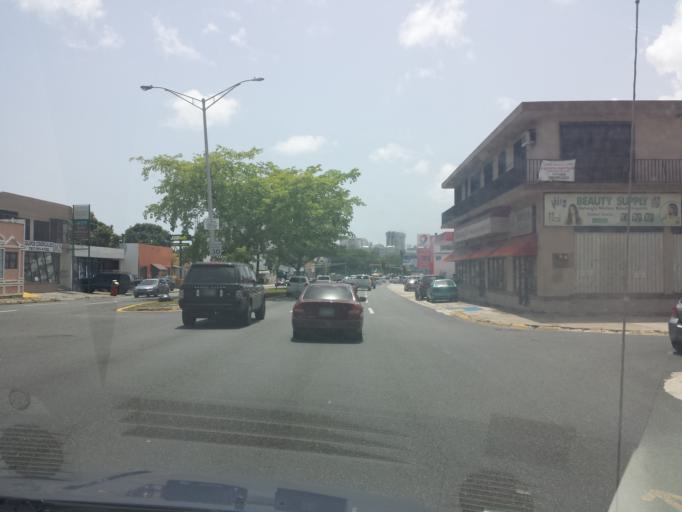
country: PR
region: Catano
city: Catano
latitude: 18.4063
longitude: -66.0776
